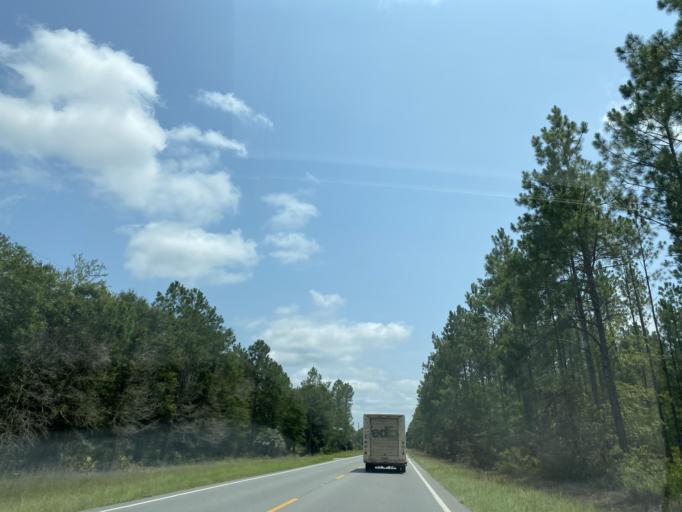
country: US
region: Georgia
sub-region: Jeff Davis County
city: Hazlehurst
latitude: 31.7427
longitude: -82.5408
